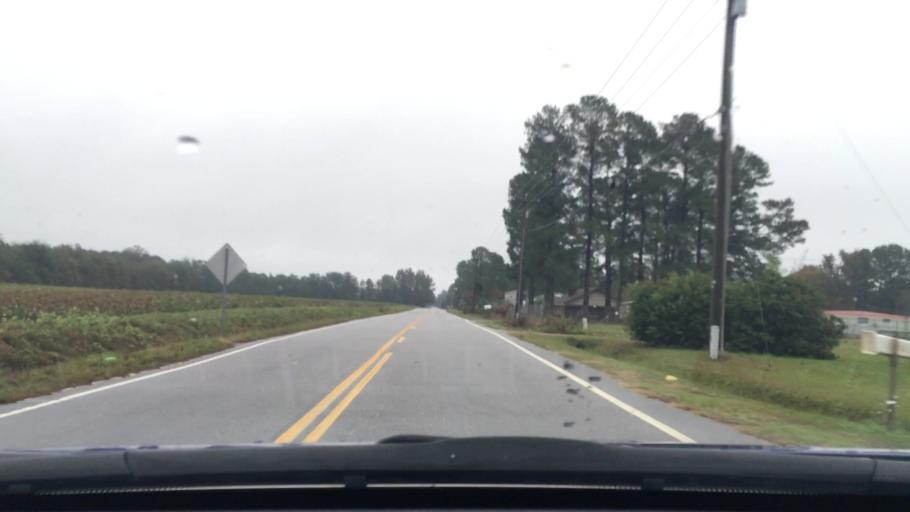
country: US
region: South Carolina
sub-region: Darlington County
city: Darlington
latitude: 34.2912
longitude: -79.9208
